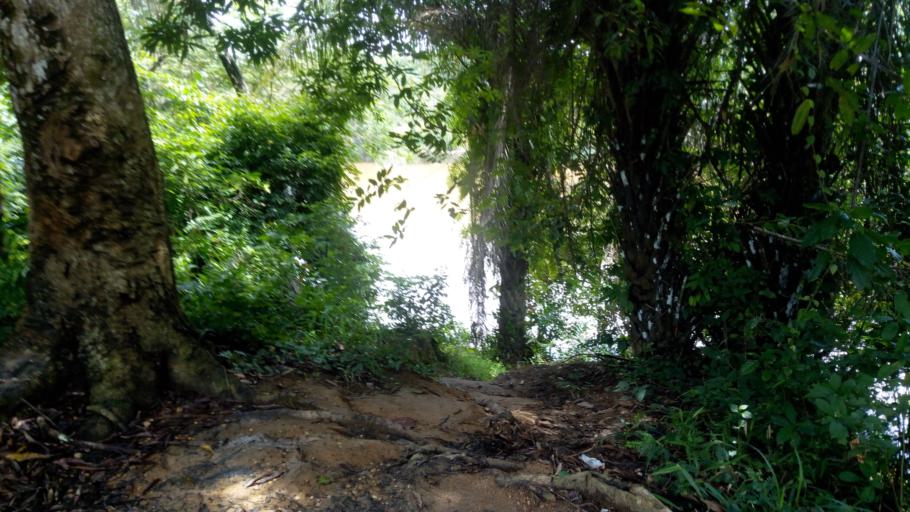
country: SL
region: Northern Province
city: Magburaka
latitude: 8.7223
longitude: -11.9609
